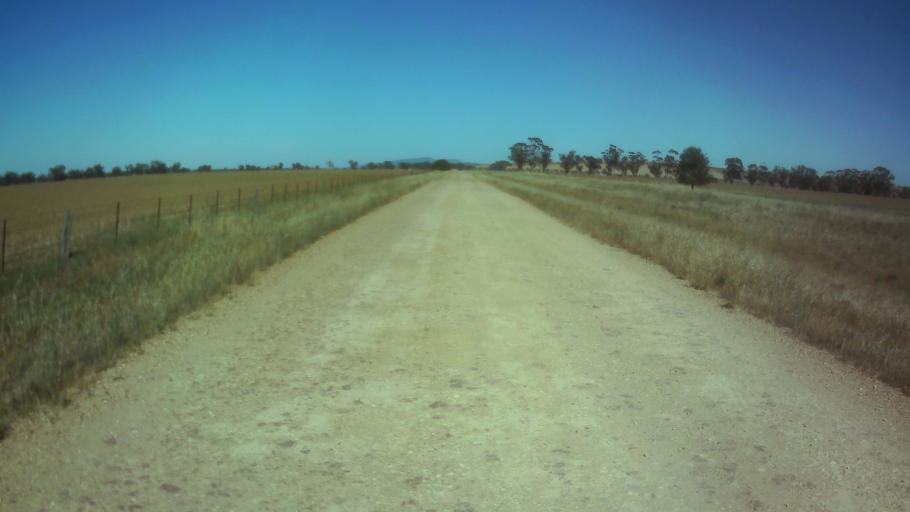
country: AU
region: New South Wales
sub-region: Weddin
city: Grenfell
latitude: -33.9963
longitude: 148.3783
